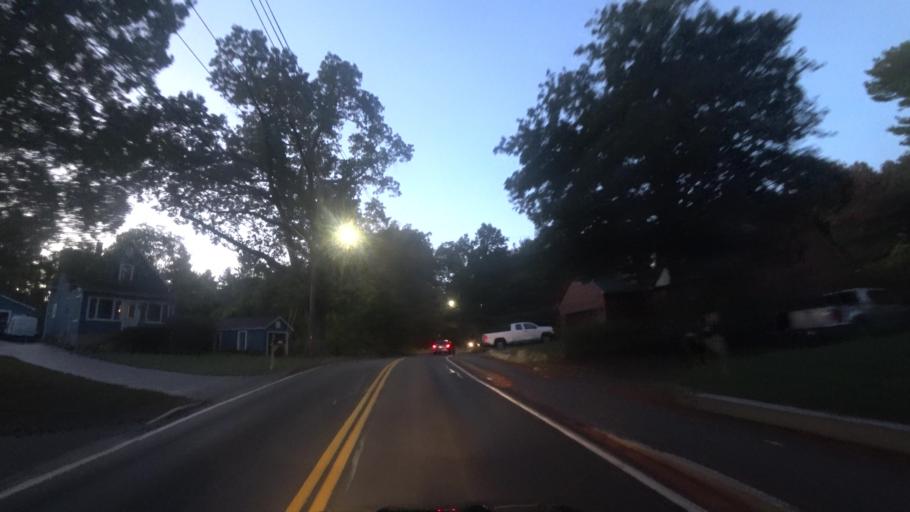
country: US
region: Massachusetts
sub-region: Middlesex County
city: Wakefield
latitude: 42.5085
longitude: -71.0446
